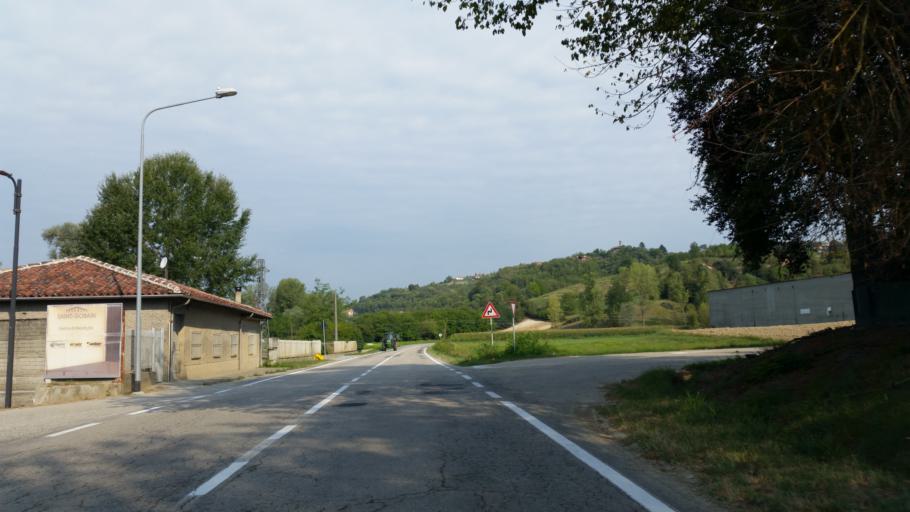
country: IT
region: Piedmont
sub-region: Provincia di Asti
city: Montiglio
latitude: 45.0709
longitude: 8.1062
